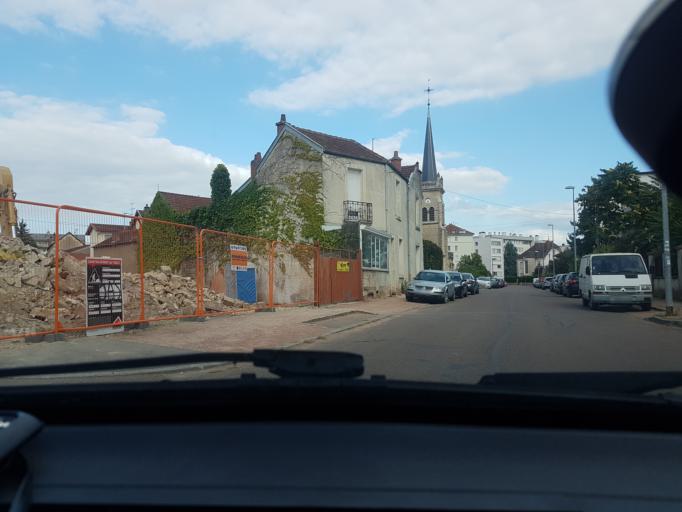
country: FR
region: Bourgogne
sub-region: Departement de la Cote-d'Or
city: Longvic
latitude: 47.3073
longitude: 5.0532
